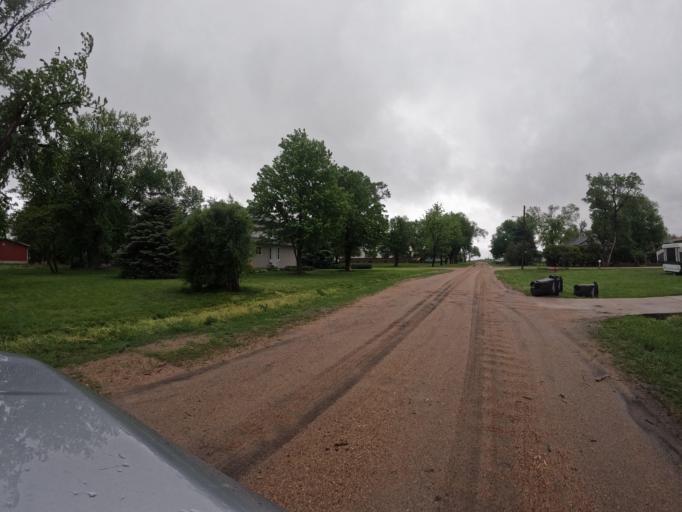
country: US
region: Nebraska
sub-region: Clay County
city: Harvard
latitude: 40.6203
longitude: -98.1014
